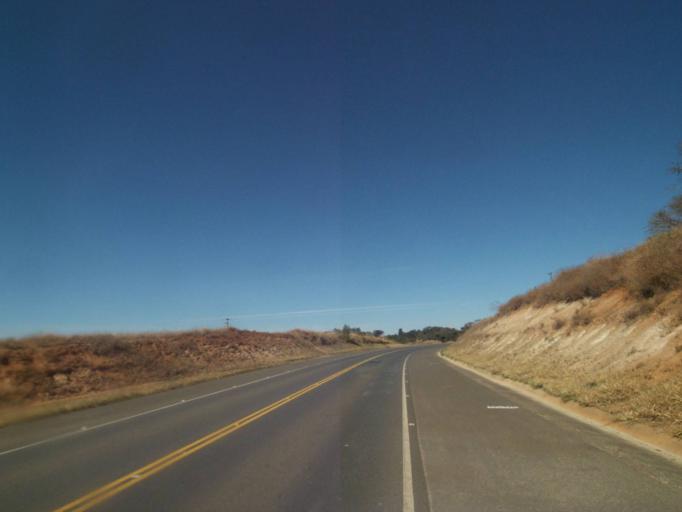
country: BR
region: Parana
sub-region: Tibagi
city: Tibagi
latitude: -24.5389
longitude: -50.4469
